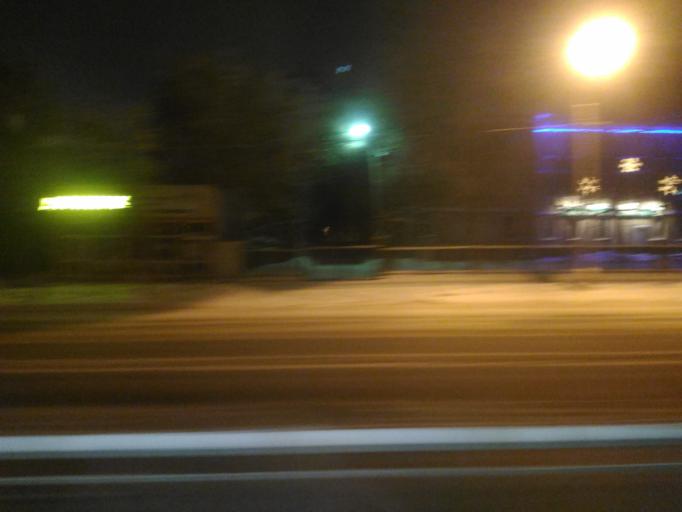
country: RU
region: Ulyanovsk
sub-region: Ulyanovskiy Rayon
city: Ulyanovsk
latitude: 54.3424
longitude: 48.3768
